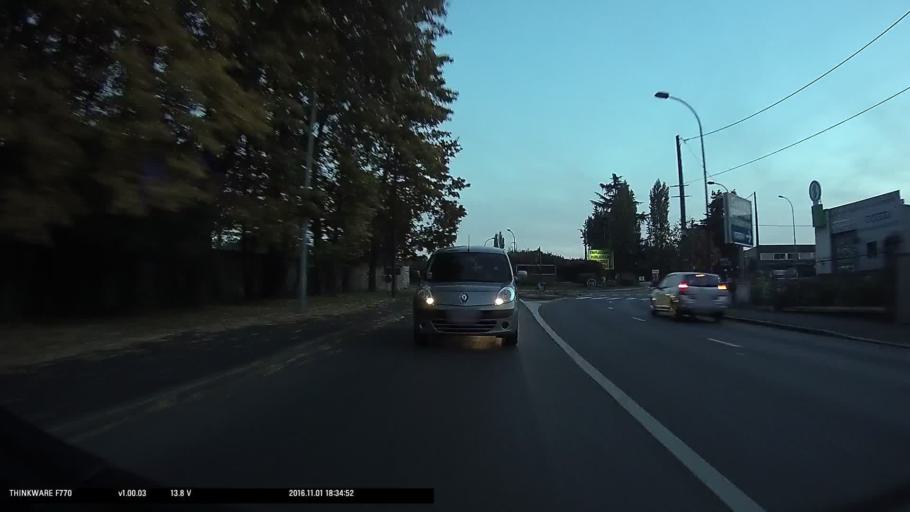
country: FR
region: Ile-de-France
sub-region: Departement de l'Essonne
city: Villemoisson-sur-Orge
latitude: 48.6625
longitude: 2.3409
